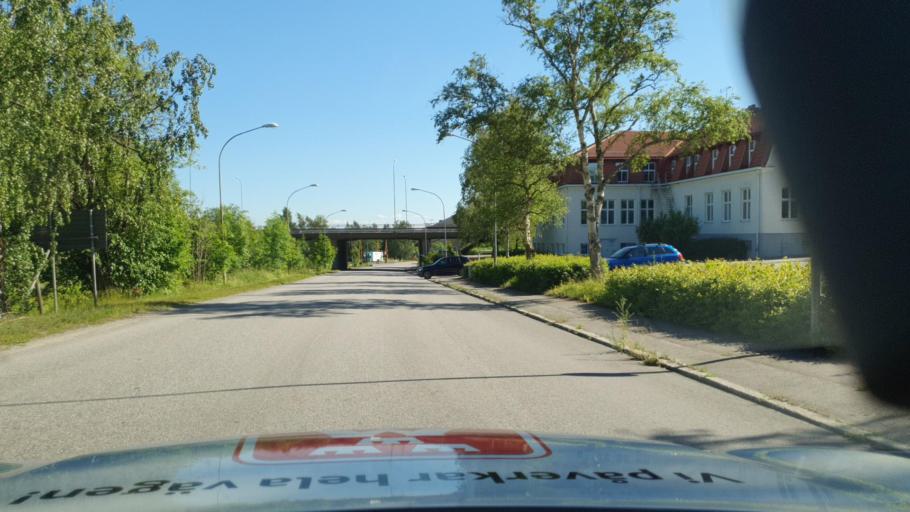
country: SE
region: OErebro
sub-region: Karlskoga Kommun
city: Karlskoga
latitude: 59.3319
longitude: 14.5490
